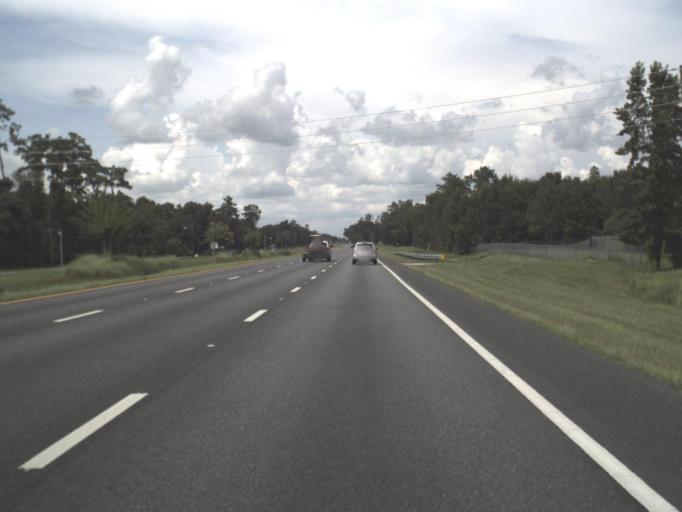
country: US
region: Florida
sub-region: Hernando County
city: South Brooksville
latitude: 28.5146
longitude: -82.4177
